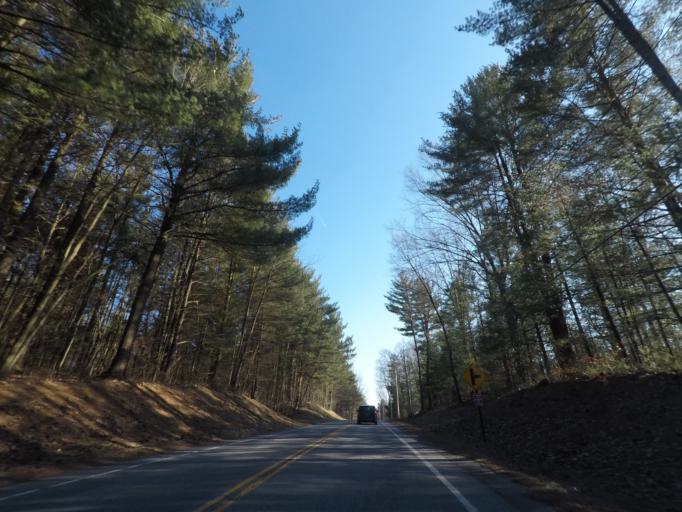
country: US
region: New York
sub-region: Schenectady County
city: Niskayuna
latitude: 42.8314
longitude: -73.7757
